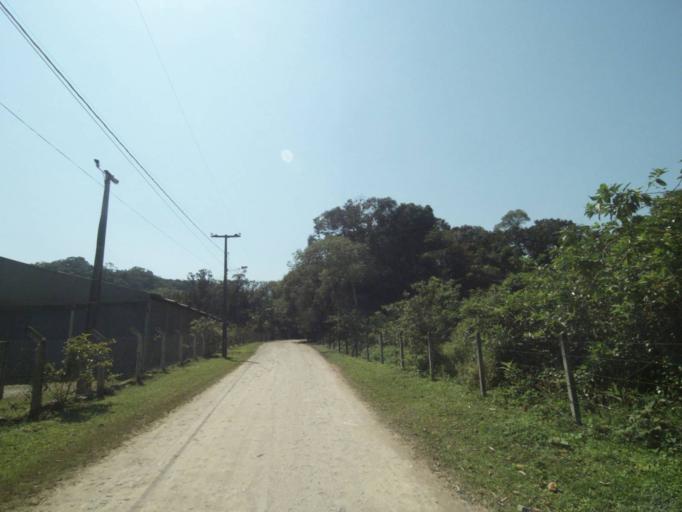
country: BR
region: Parana
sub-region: Paranagua
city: Paranagua
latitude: -25.5503
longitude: -48.5911
